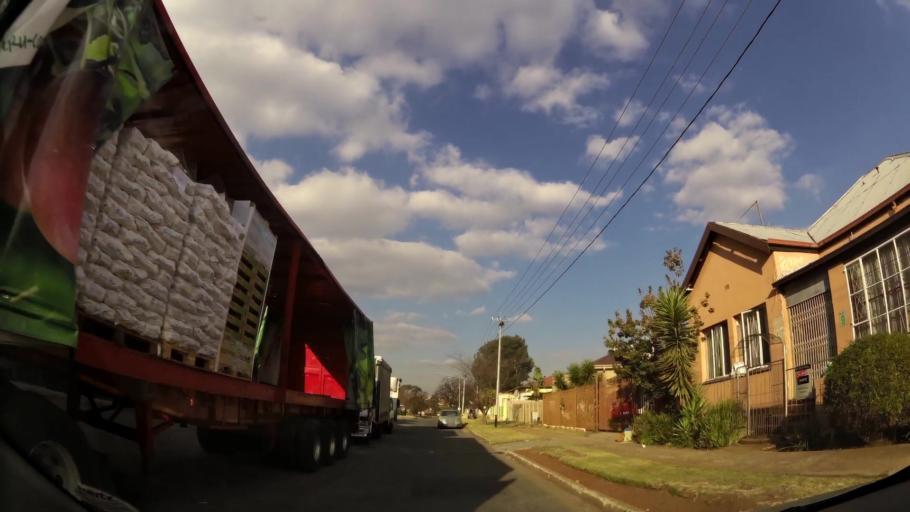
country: ZA
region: Gauteng
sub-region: West Rand District Municipality
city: Krugersdorp
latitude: -26.0990
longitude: 27.7609
